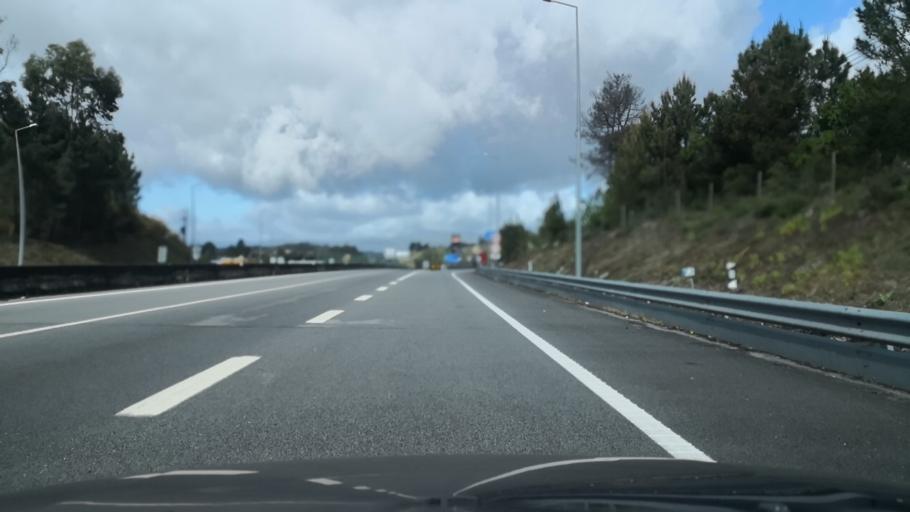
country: PT
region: Viseu
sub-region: Viseu
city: Viseu
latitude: 40.6240
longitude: -7.9290
